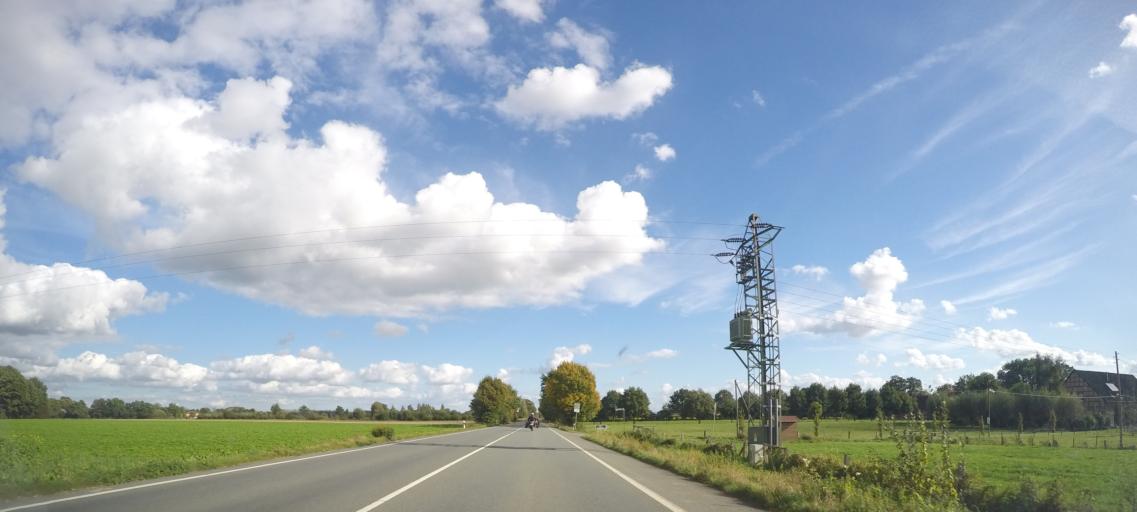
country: DE
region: North Rhine-Westphalia
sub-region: Regierungsbezirk Arnsberg
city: Welver
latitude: 51.6726
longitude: 8.0157
